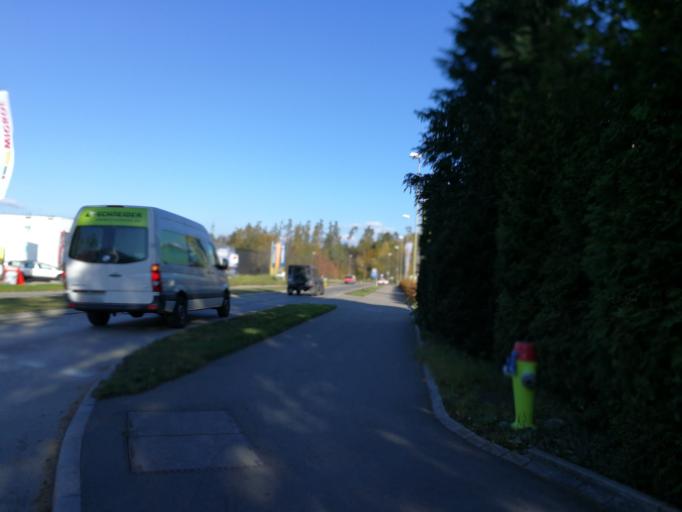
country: CH
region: Zurich
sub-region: Bezirk Uster
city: Egg
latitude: 47.3039
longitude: 8.6907
